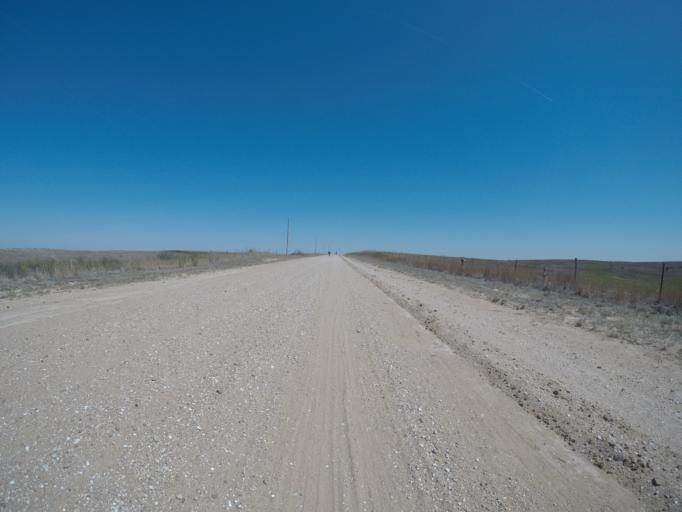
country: US
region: Kansas
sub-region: Pratt County
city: Pratt
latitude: 37.4100
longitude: -98.8400
